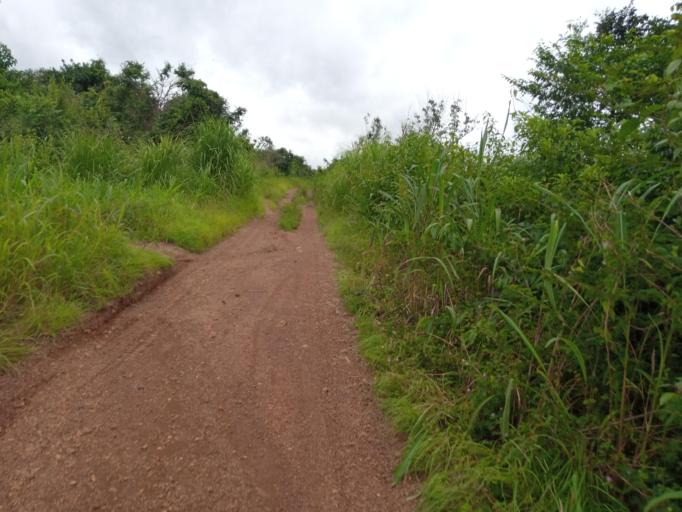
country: SL
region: Southern Province
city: Largo
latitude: 8.1992
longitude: -12.0522
